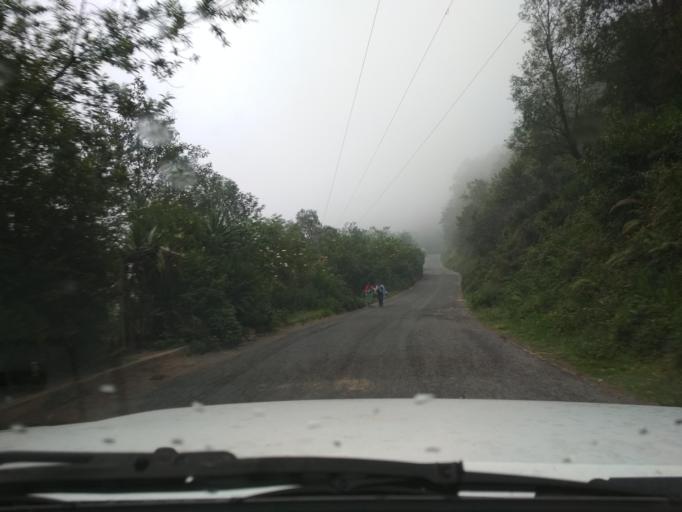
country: MX
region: Veracruz
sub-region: La Perla
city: Metlac Hernandez (Metlac Primero)
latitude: 18.9528
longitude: -97.1729
